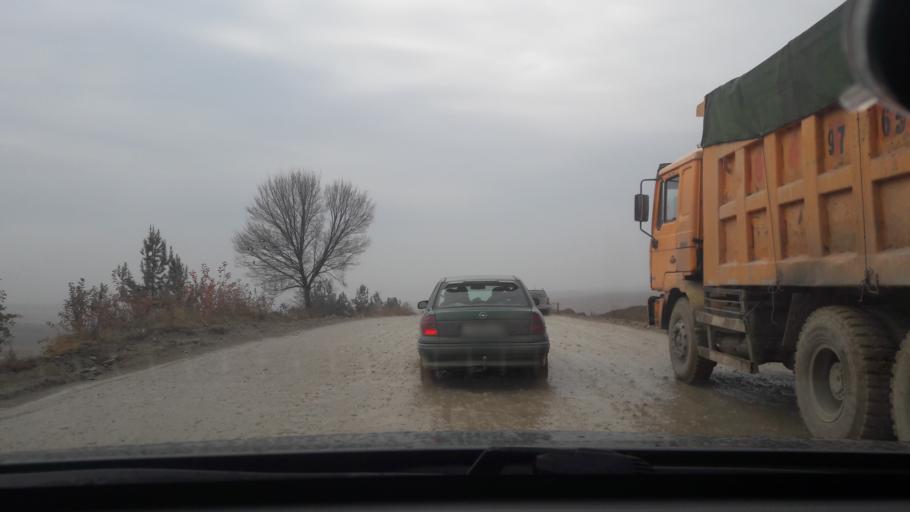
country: TJ
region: Dushanbe
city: Boshkengash
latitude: 38.3256
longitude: 68.7099
